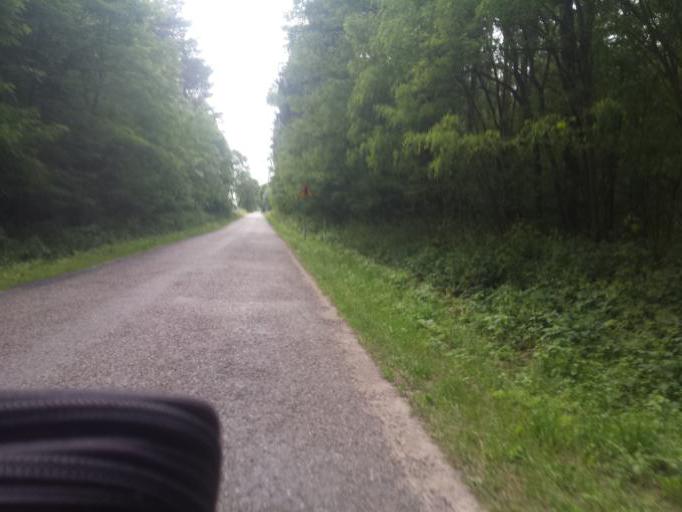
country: PL
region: Warmian-Masurian Voivodeship
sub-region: Powiat ilawski
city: Ilawa
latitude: 53.5275
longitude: 19.5240
